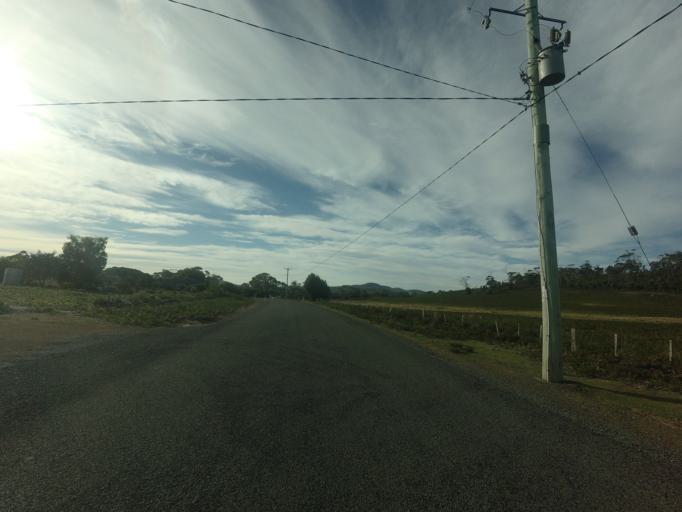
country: AU
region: Tasmania
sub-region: Sorell
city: Sorell
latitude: -42.9677
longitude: 147.8318
